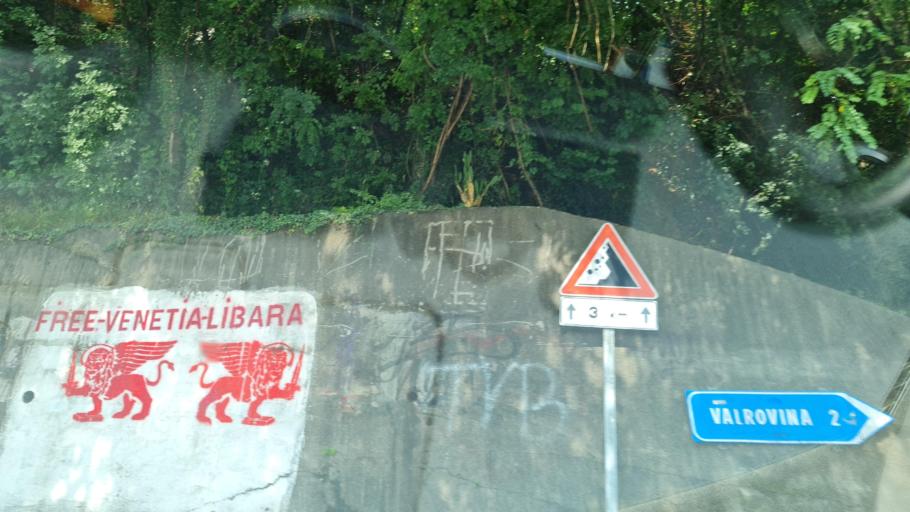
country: IT
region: Veneto
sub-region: Provincia di Vicenza
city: Marostica
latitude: 45.7816
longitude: 11.6783
